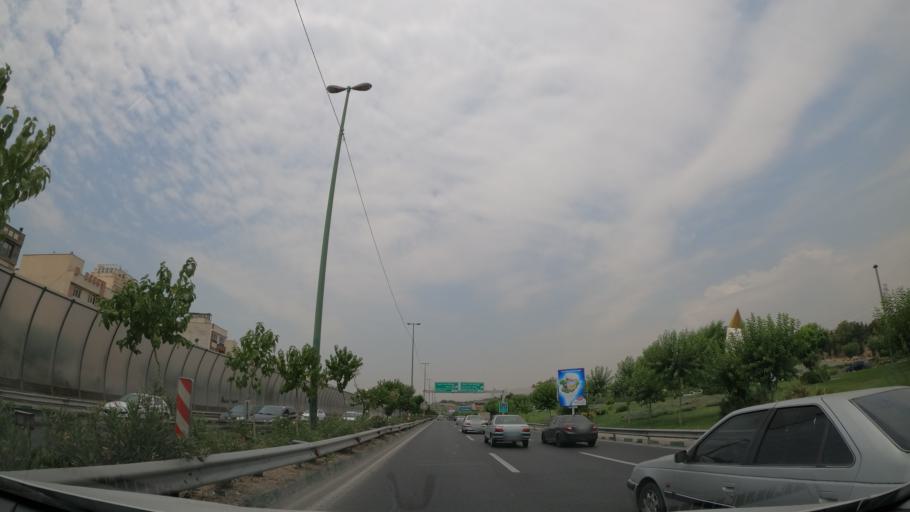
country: IR
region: Tehran
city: Tehran
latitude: 35.7394
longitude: 51.3569
